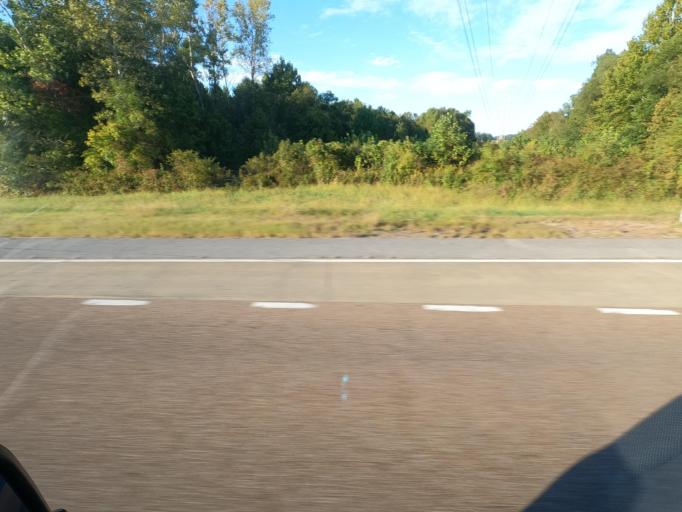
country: US
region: Tennessee
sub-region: Shelby County
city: Millington
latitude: 35.3084
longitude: -89.8315
